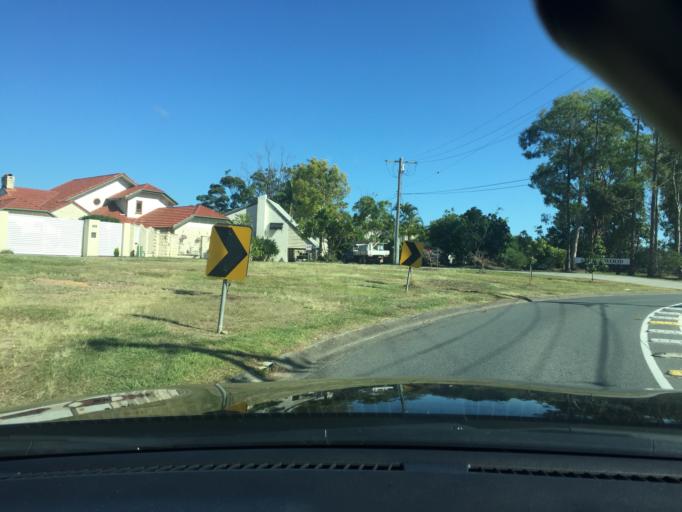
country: AU
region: Queensland
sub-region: Logan
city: Slacks Creek
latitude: -27.6278
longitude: 153.1480
